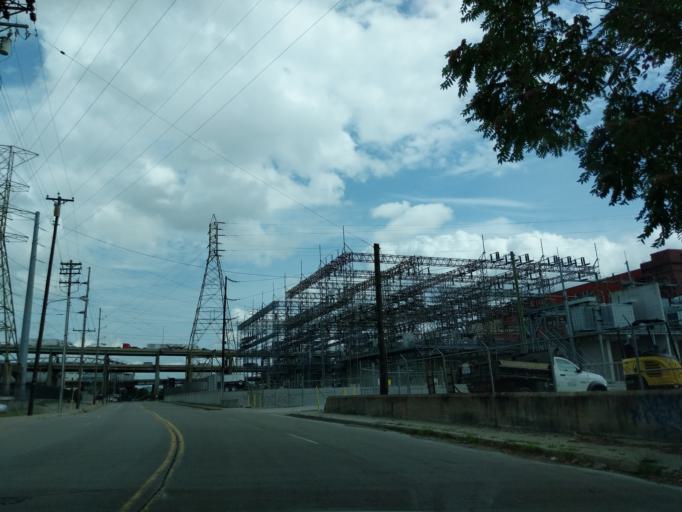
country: US
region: Kentucky
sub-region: Kenton County
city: Covington
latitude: 39.0945
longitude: -84.5258
